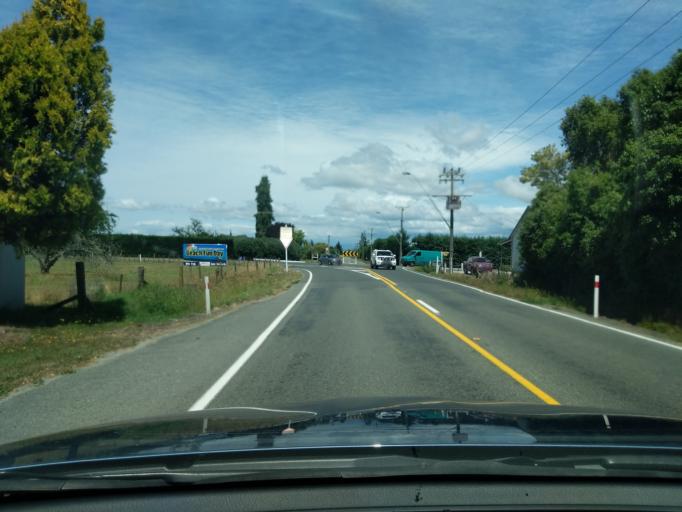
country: NZ
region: Tasman
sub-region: Tasman District
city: Motueka
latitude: -41.0900
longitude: 172.9967
